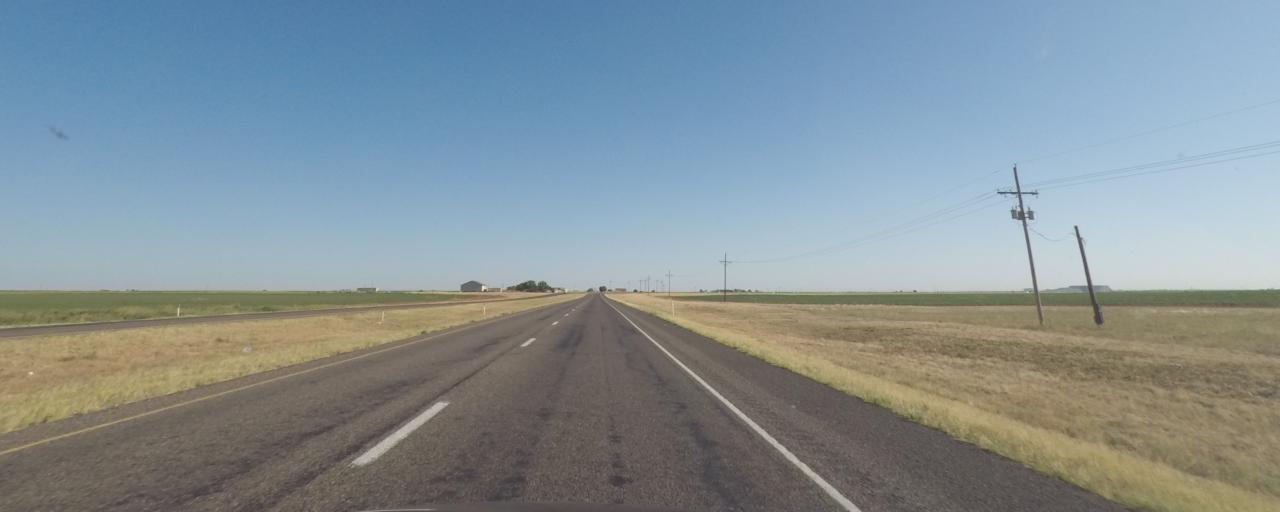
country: US
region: Texas
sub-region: Gaines County
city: Seagraves
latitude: 32.8649
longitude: -102.6402
